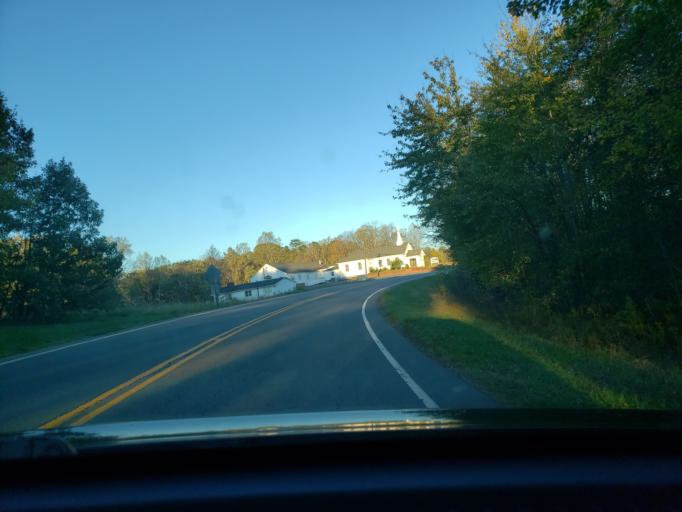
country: US
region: North Carolina
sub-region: Stokes County
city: Danbury
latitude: 36.3221
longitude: -80.2330
